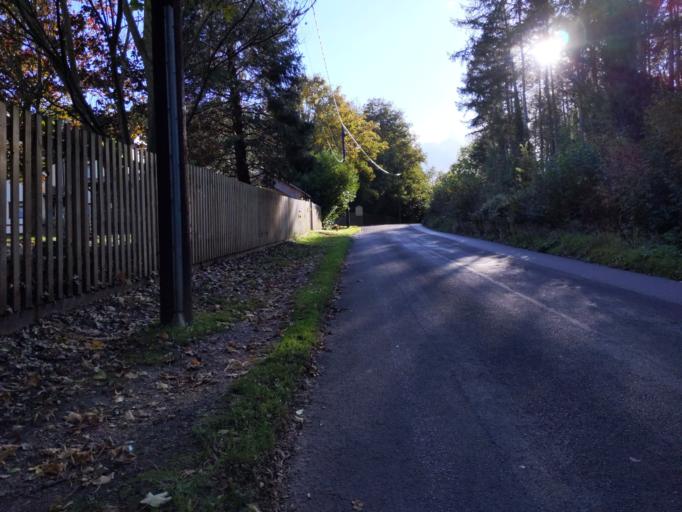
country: GB
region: England
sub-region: Oxfordshire
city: Radley
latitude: 51.7114
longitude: -1.2492
